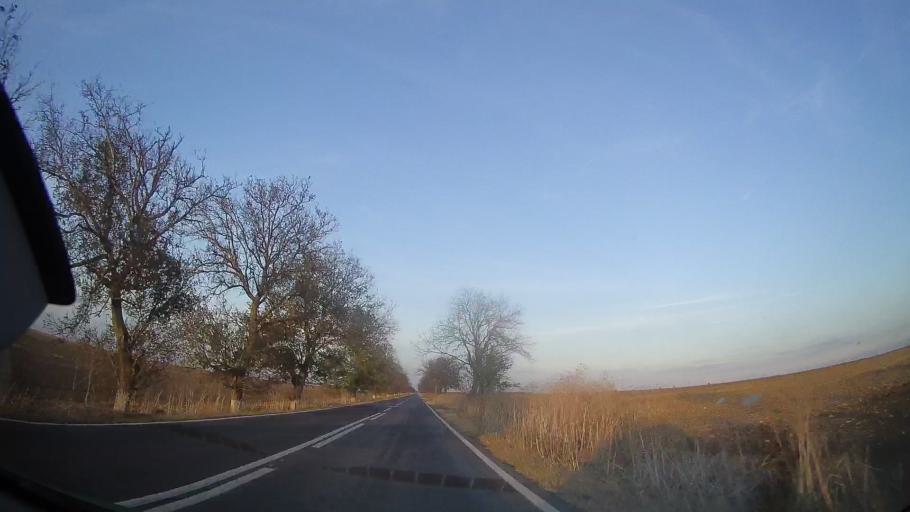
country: RO
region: Constanta
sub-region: Comuna Topraisar
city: Topraisar
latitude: 43.9892
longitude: 28.4233
